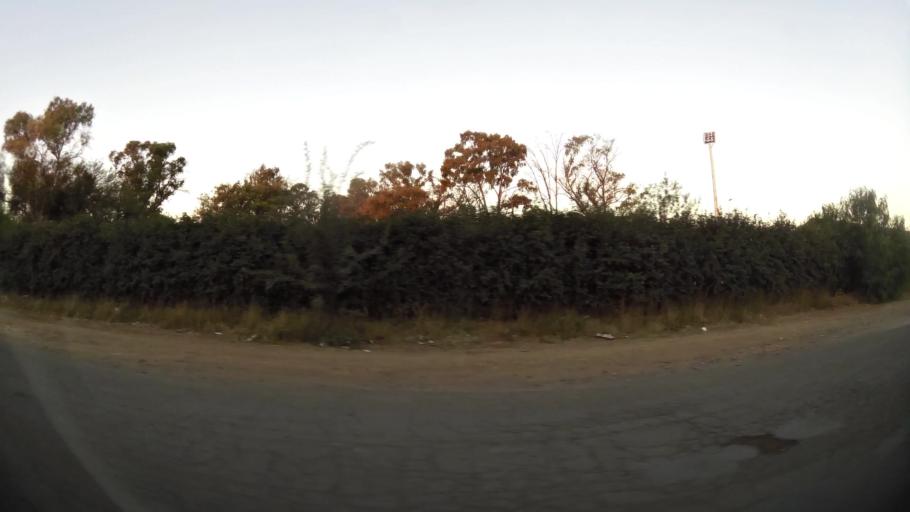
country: ZA
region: Northern Cape
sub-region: Frances Baard District Municipality
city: Kimberley
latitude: -28.7252
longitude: 24.7757
